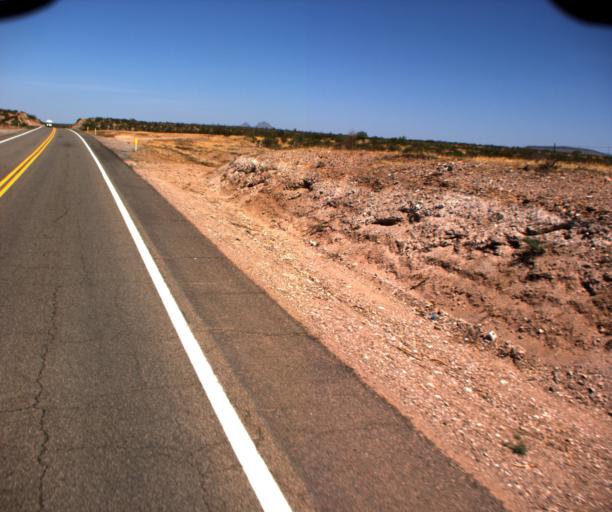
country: US
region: Arizona
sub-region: Graham County
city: Bylas
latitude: 33.2192
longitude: -110.2186
